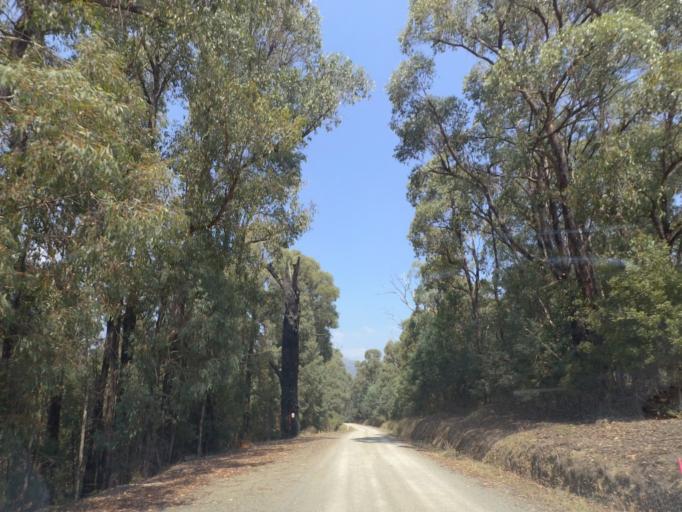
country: AU
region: Victoria
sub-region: Yarra Ranges
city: Millgrove
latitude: -37.5421
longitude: 145.7207
